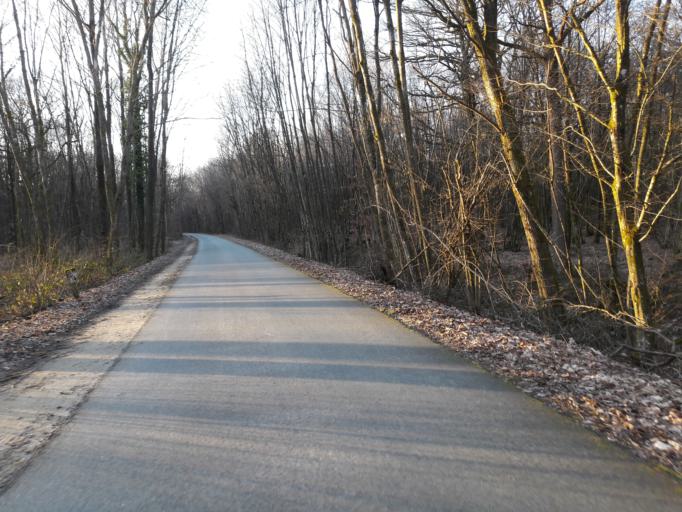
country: BE
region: Wallonia
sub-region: Province du Hainaut
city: Momignies
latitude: 50.0239
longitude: 4.2134
